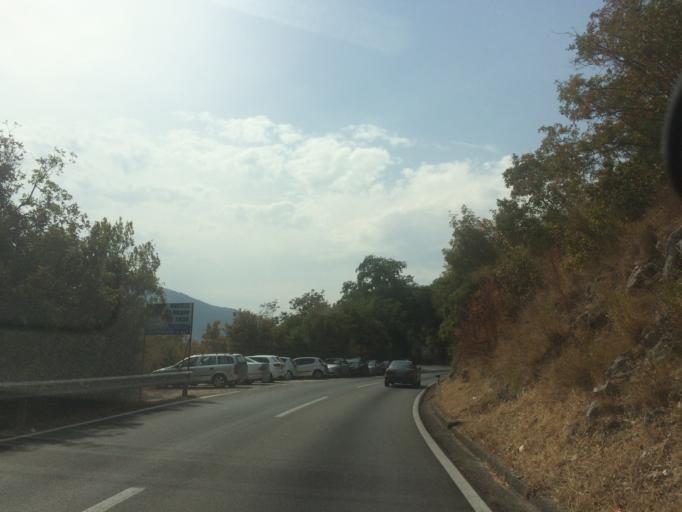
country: ME
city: Dobrota
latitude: 42.4843
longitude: 18.7366
